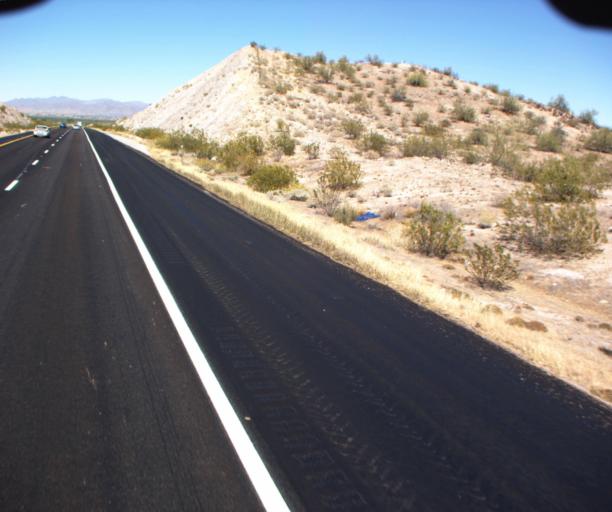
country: US
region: Arizona
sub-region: Maricopa County
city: Buckeye
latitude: 33.2991
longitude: -112.6270
